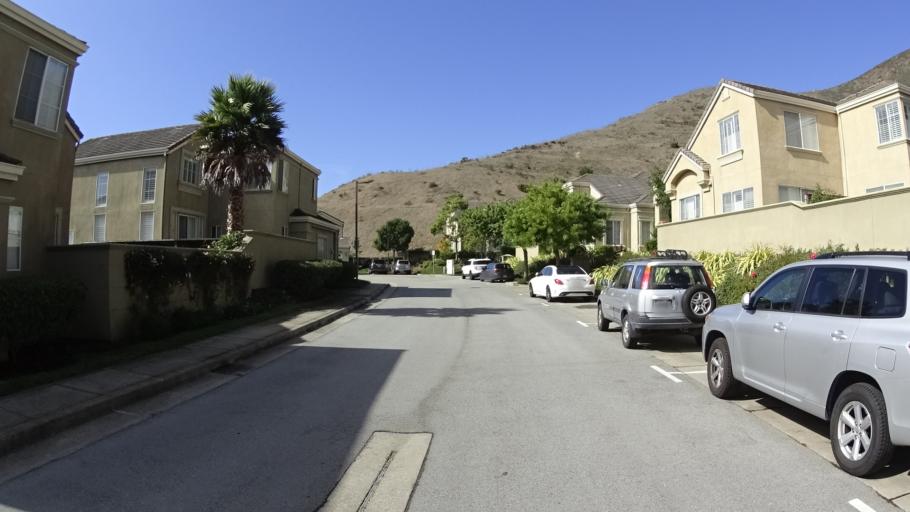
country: US
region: California
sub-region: San Mateo County
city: South San Francisco
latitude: 37.6717
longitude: -122.4178
